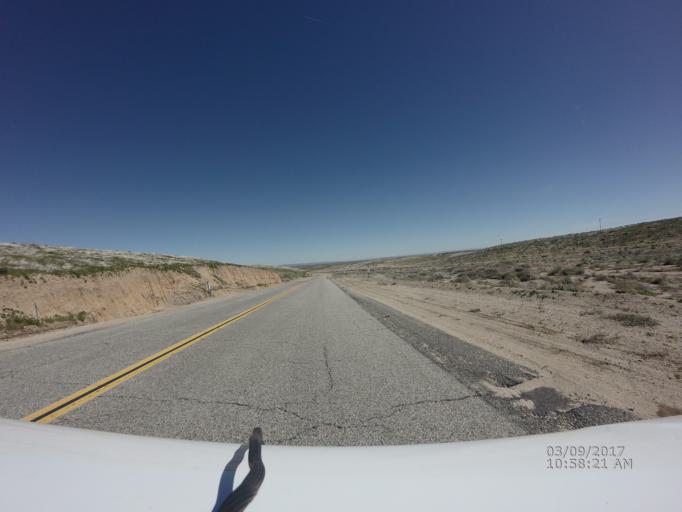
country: US
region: California
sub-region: Los Angeles County
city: Green Valley
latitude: 34.6949
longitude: -118.3827
